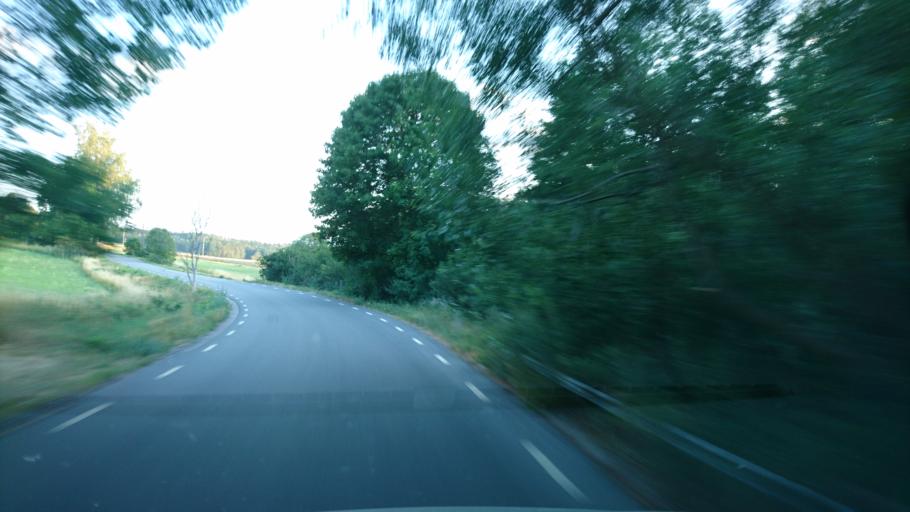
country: SE
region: Uppsala
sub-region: Uppsala Kommun
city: Saevja
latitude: 59.7891
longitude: 17.6653
